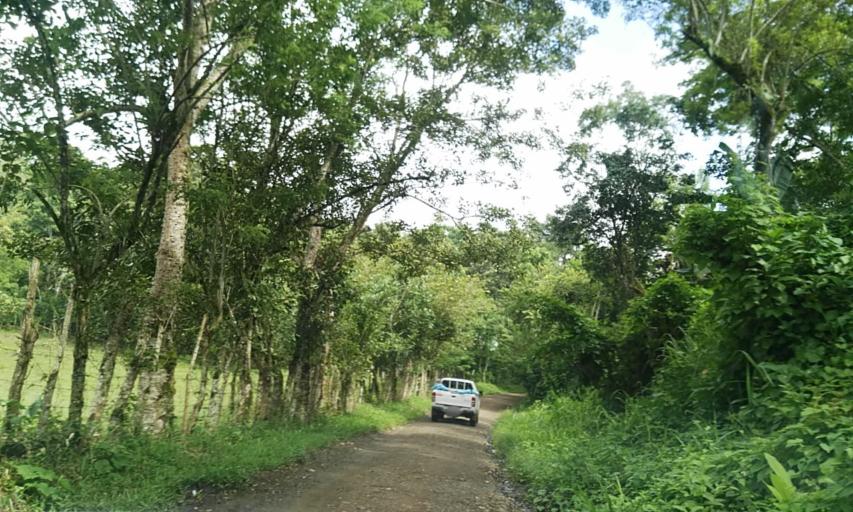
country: NI
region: Matagalpa
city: San Ramon
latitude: 12.9835
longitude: -85.8459
